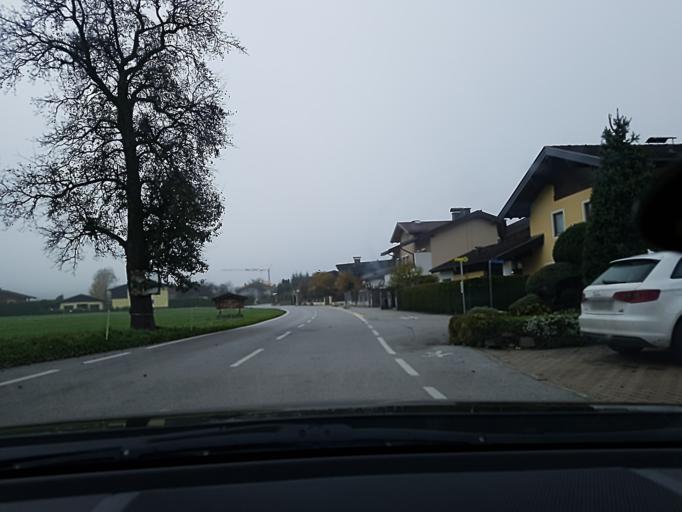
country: AT
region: Salzburg
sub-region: Politischer Bezirk Sankt Johann im Pongau
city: Sankt Johann im Pongau
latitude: 47.3715
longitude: 13.2125
